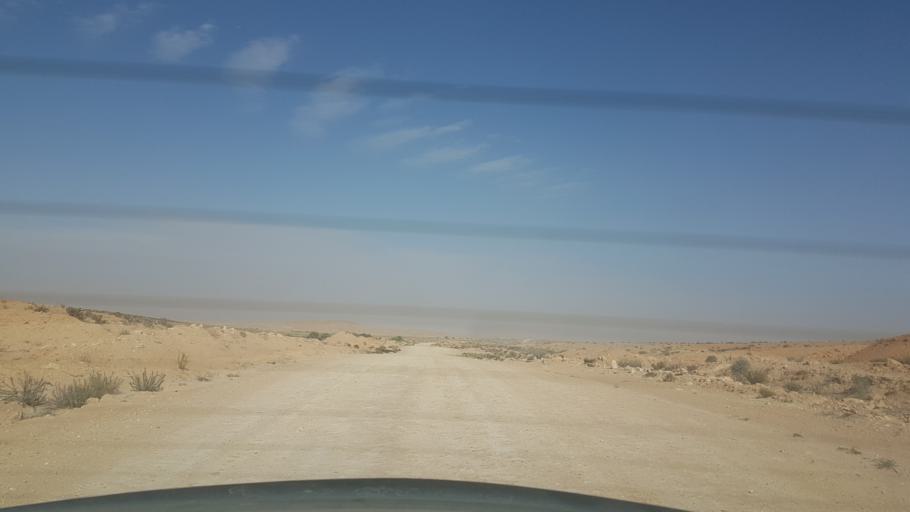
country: TN
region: Qabis
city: El Hamma
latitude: 33.6599
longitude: 9.7346
